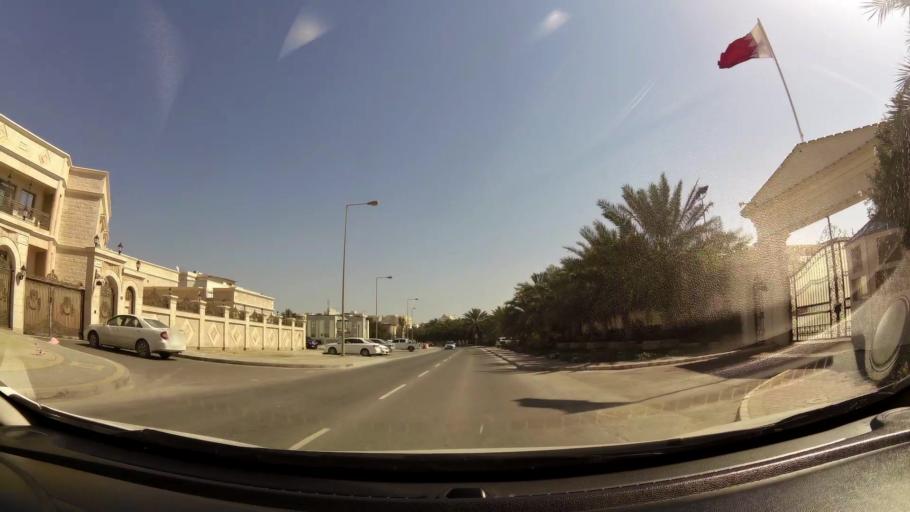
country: BH
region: Manama
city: Manama
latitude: 26.2092
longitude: 50.5798
